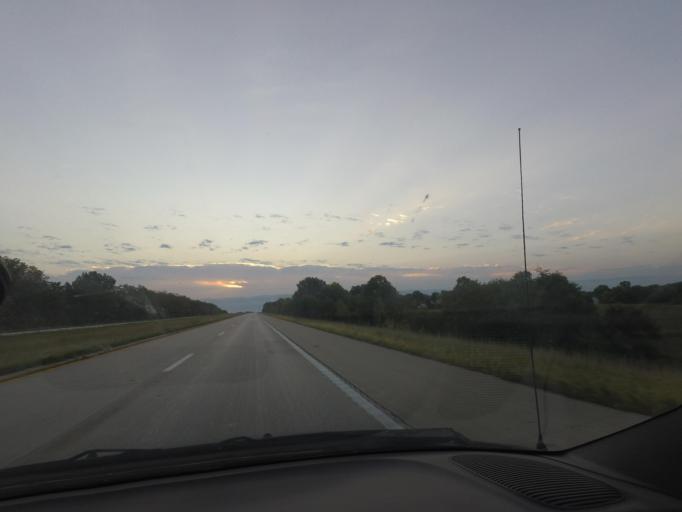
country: US
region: Missouri
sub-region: Macon County
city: Macon
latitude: 39.7553
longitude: -92.4462
